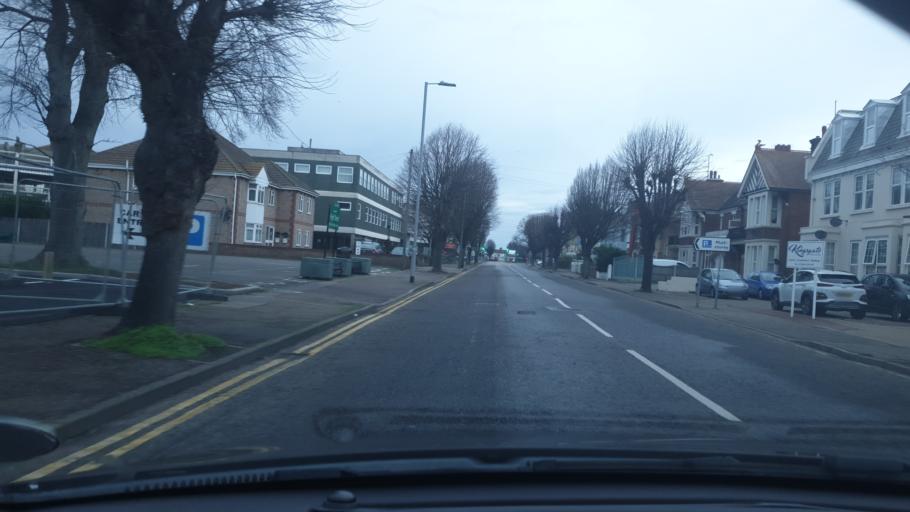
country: GB
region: England
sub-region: Essex
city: Clacton-on-Sea
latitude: 51.7914
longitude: 1.1557
